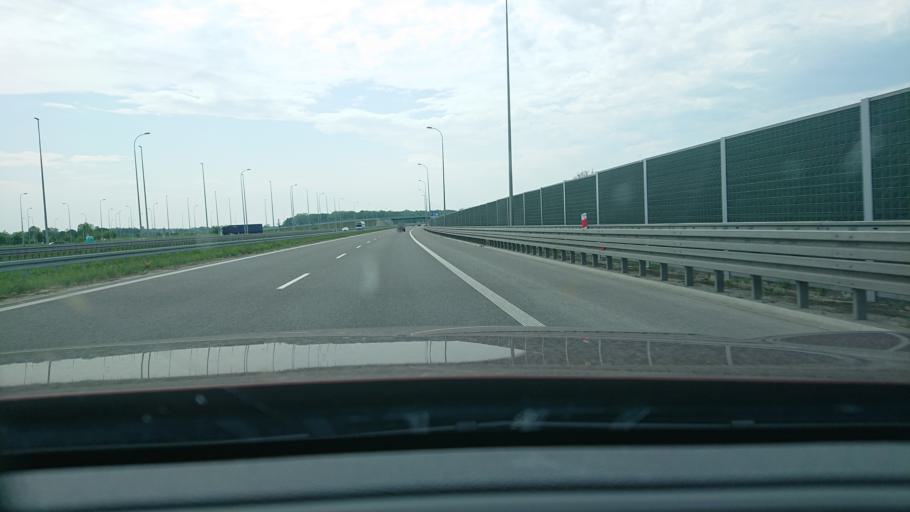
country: PL
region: Subcarpathian Voivodeship
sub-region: Powiat lancucki
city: Czarna
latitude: 50.0900
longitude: 22.1671
